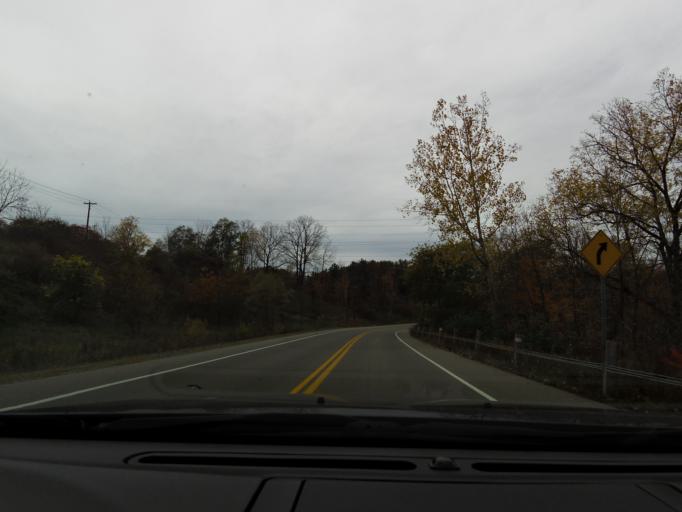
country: CA
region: Ontario
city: Hamilton
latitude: 43.3012
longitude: -79.8860
